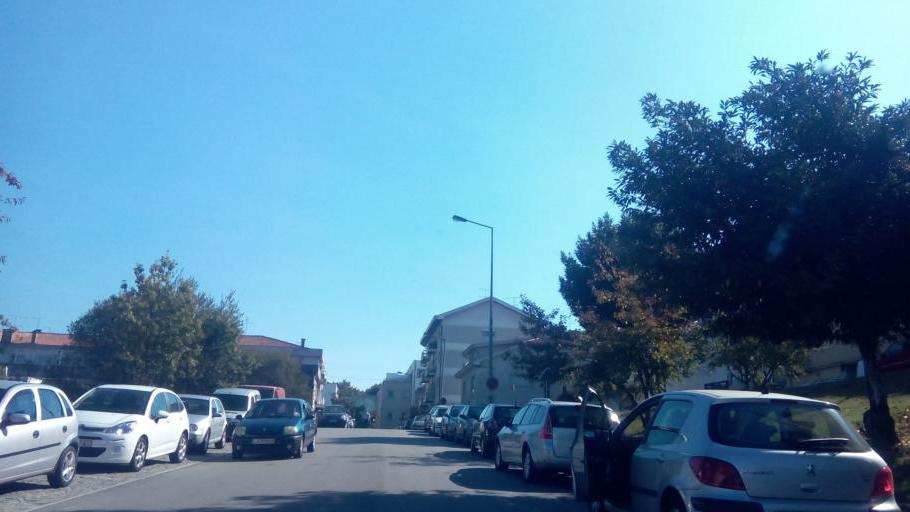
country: PT
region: Porto
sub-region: Paredes
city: Paredes
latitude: 41.2098
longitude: -8.3350
